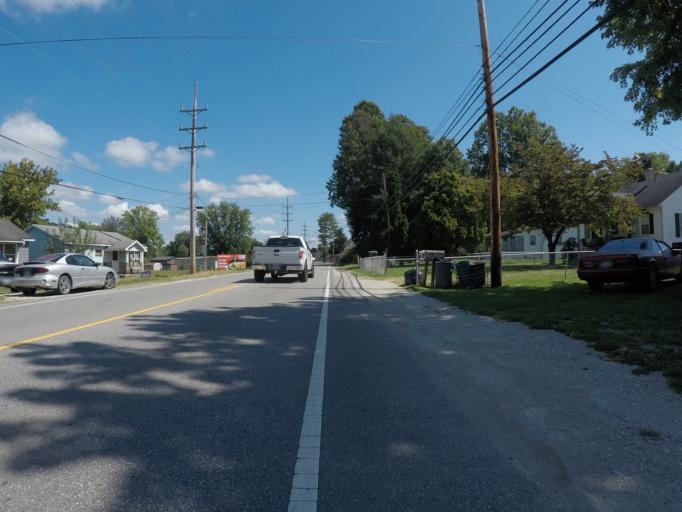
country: US
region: Ohio
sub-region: Lawrence County
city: Burlington
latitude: 38.4095
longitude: -82.5212
